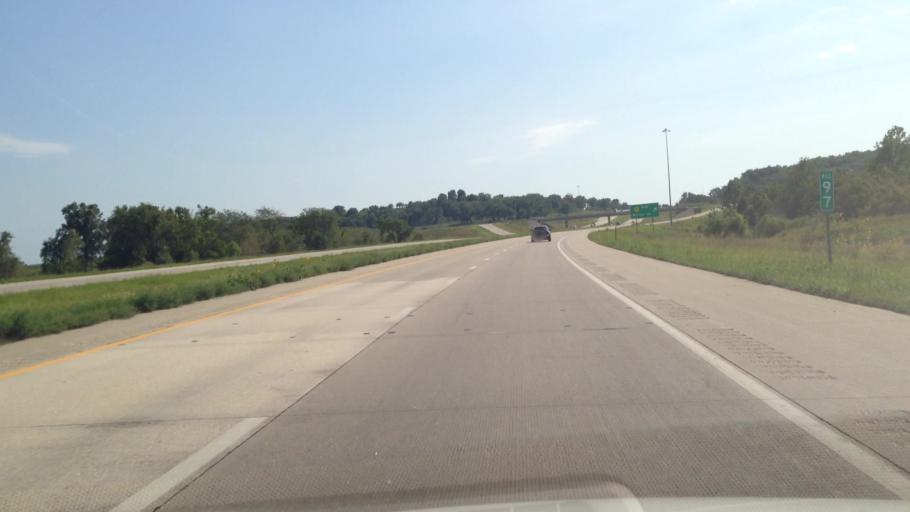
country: US
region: Kansas
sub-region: Linn County
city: Pleasanton
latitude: 38.2679
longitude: -94.6694
